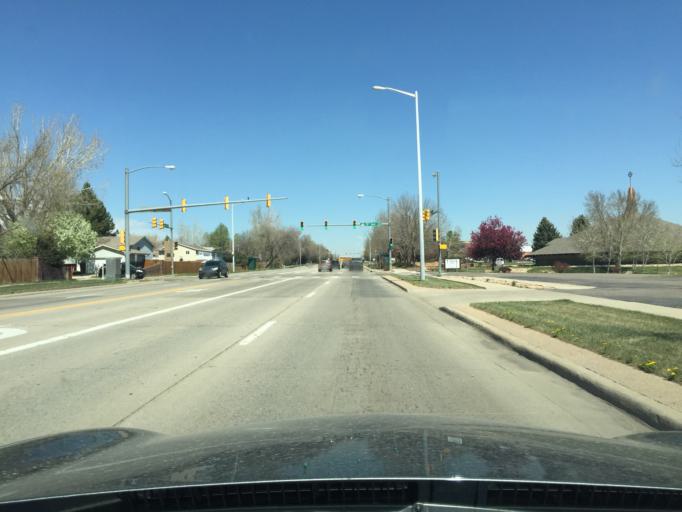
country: US
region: Colorado
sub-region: Boulder County
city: Longmont
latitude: 40.1844
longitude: -105.1308
